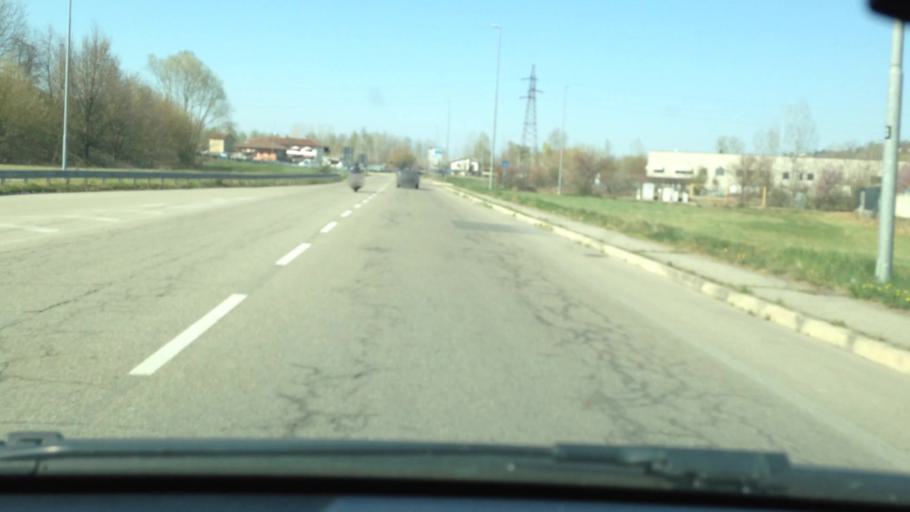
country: IT
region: Piedmont
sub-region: Provincia di Asti
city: Asti
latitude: 44.9184
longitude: 8.2286
